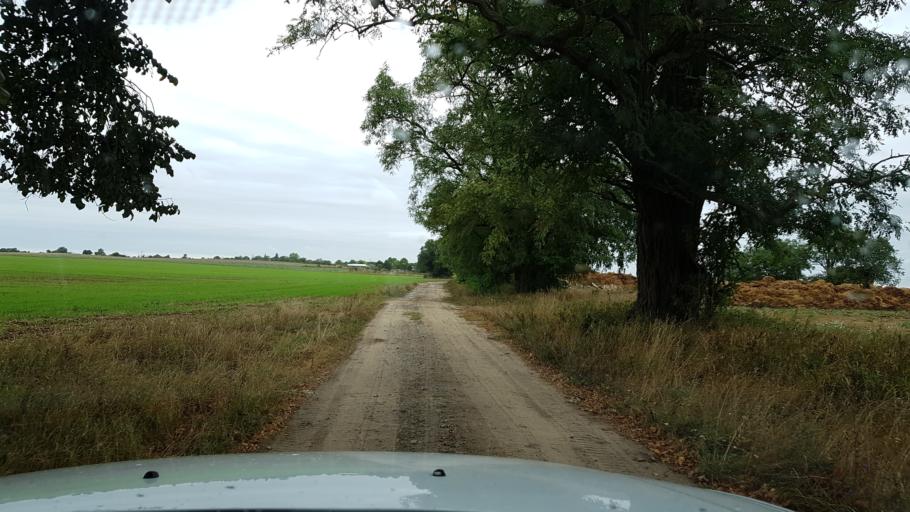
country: PL
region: West Pomeranian Voivodeship
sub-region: Powiat gryfinski
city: Moryn
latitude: 52.8395
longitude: 14.3004
